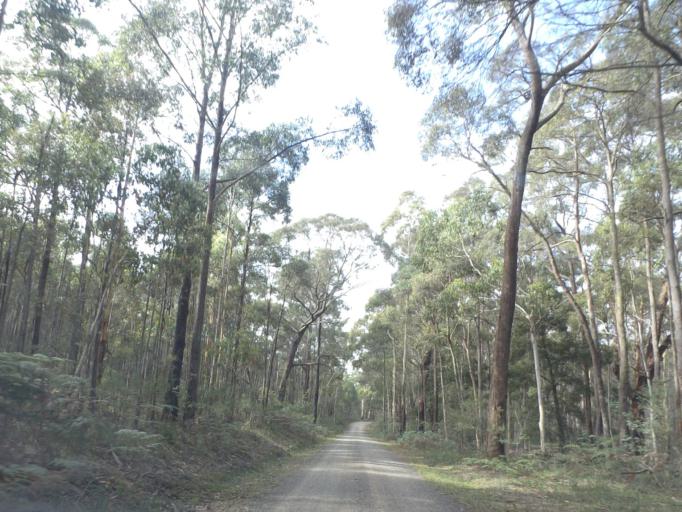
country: AU
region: Victoria
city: Brown Hill
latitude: -37.4930
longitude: 144.1753
